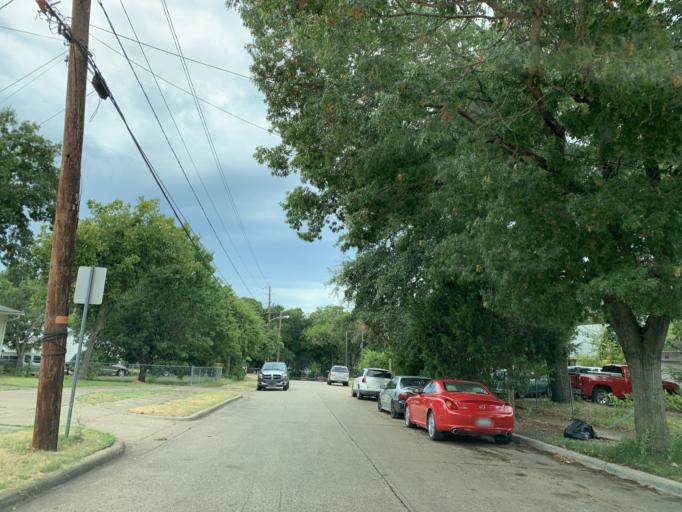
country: US
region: Texas
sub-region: Dallas County
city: Duncanville
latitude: 32.6692
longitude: -96.8340
